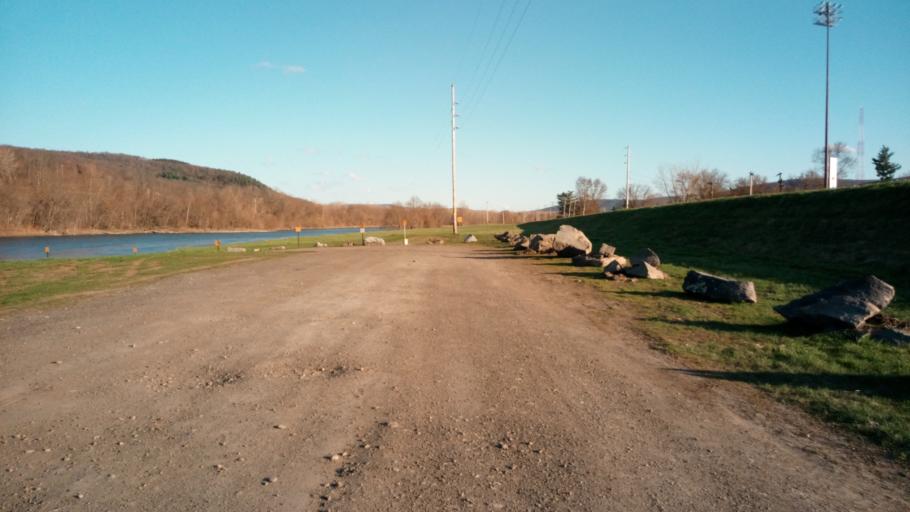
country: US
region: New York
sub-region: Chemung County
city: Elmira
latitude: 42.0808
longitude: -76.7796
